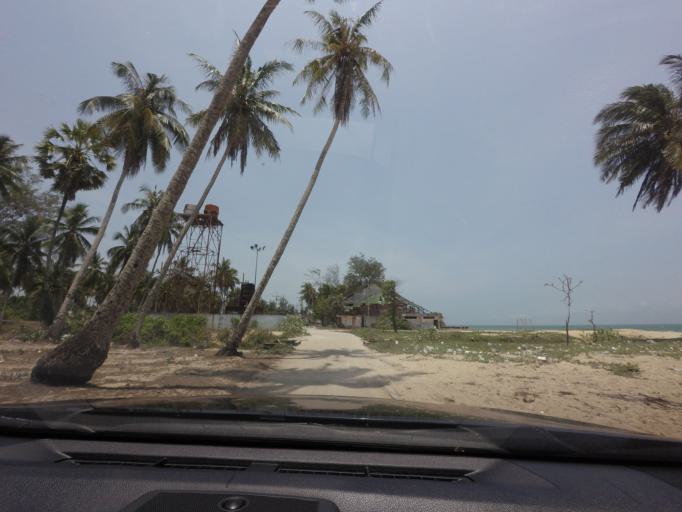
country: TH
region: Pattani
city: Yaring
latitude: 6.8981
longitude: 101.3743
